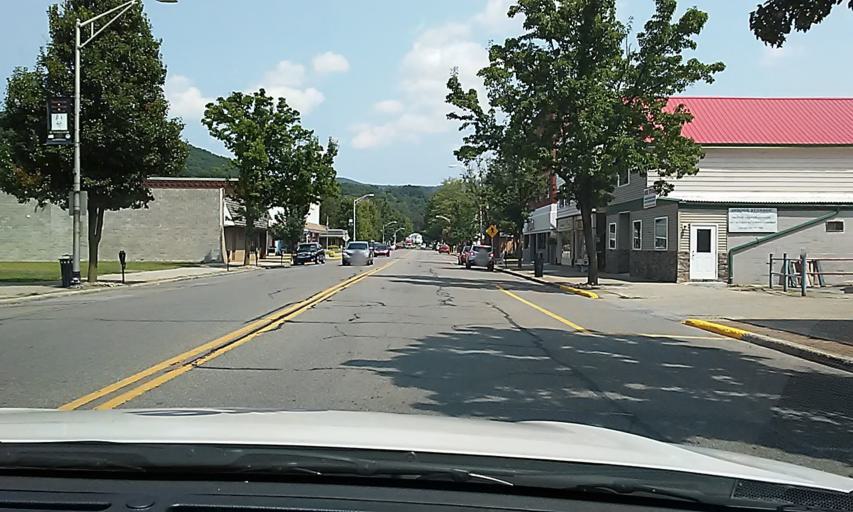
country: US
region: Pennsylvania
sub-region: Cameron County
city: Emporium
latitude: 41.5116
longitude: -78.2366
